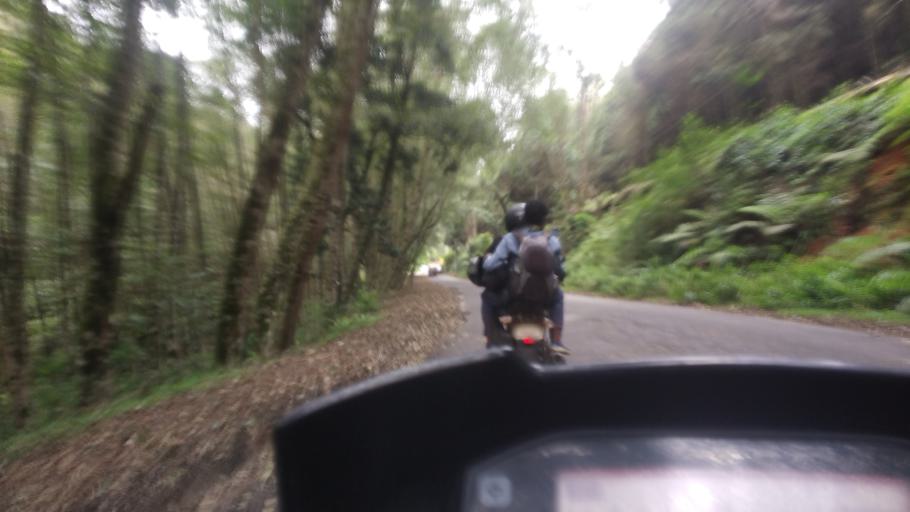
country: IN
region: Kerala
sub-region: Idukki
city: Munnar
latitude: 10.0661
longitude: 77.0987
